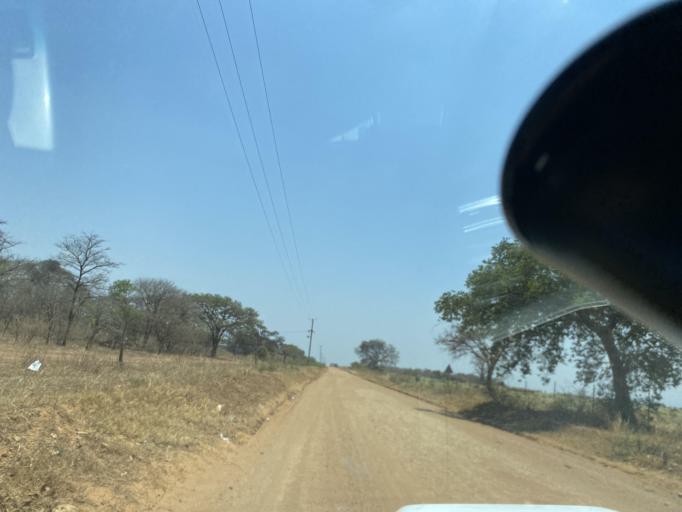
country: ZM
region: Lusaka
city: Lusaka
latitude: -15.4347
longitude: 28.0773
